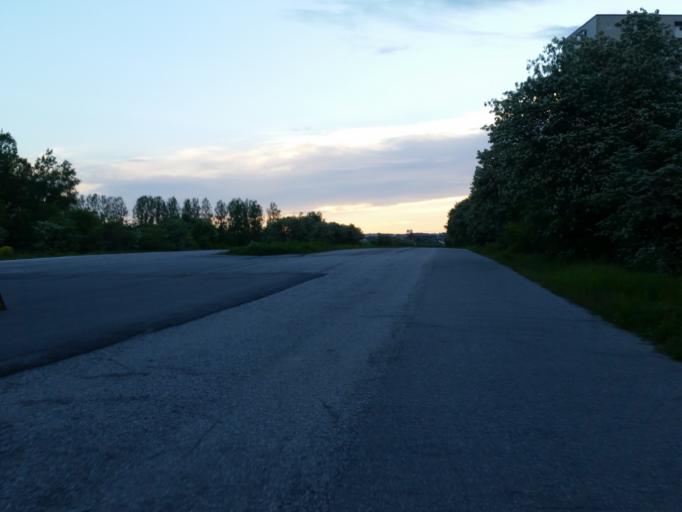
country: SE
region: Stockholm
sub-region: Stockholms Kommun
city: Arsta
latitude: 59.2919
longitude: 18.0527
